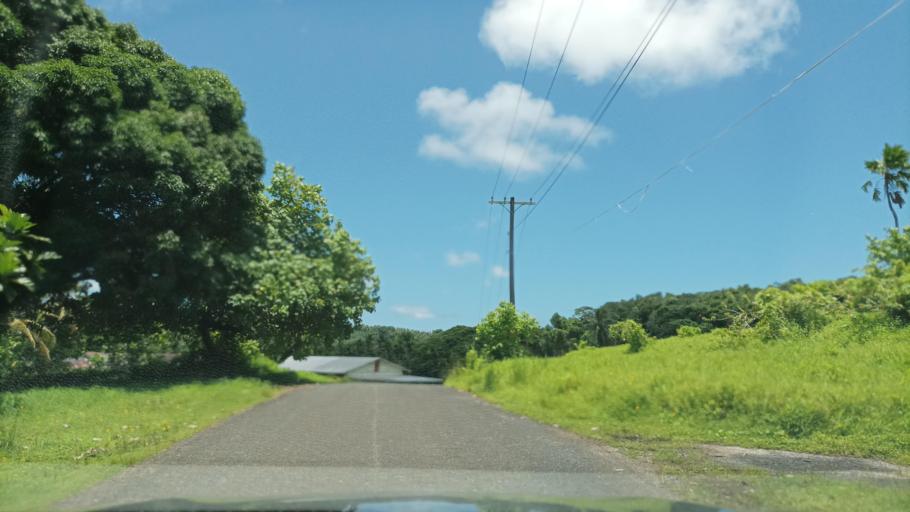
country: FM
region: Pohnpei
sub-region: Madolenihm Municipality
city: Madolenihm Municipality Government
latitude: 6.8427
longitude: 158.3071
